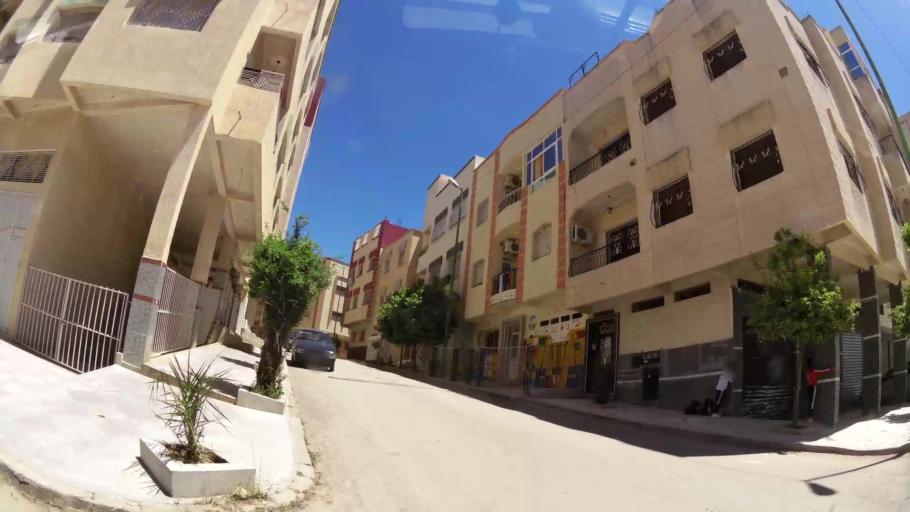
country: MA
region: Meknes-Tafilalet
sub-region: Meknes
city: Meknes
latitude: 33.8567
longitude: -5.5535
